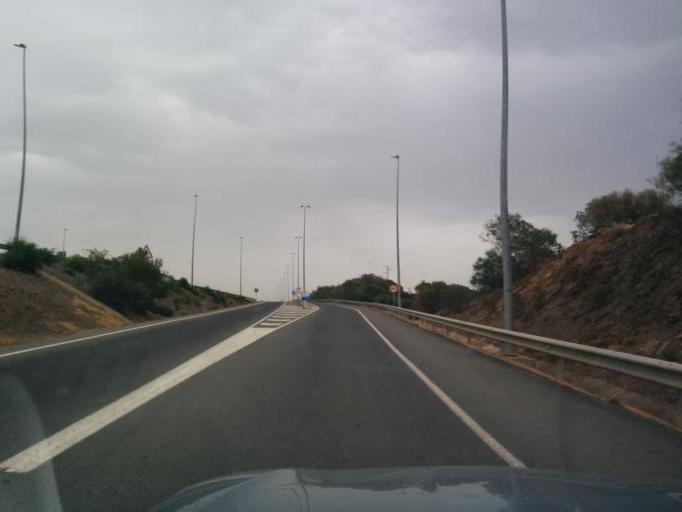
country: ES
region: Andalusia
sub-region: Provincia de Huelva
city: Ayamonte
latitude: 37.2384
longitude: -7.4032
